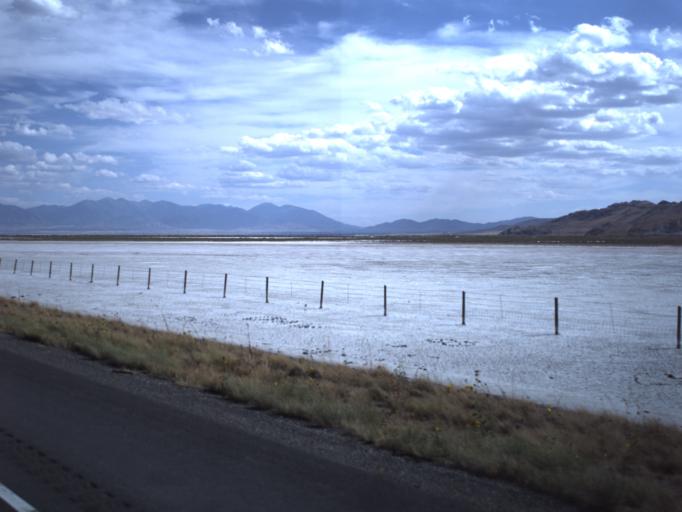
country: US
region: Utah
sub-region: Tooele County
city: Grantsville
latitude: 40.7275
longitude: -112.5809
